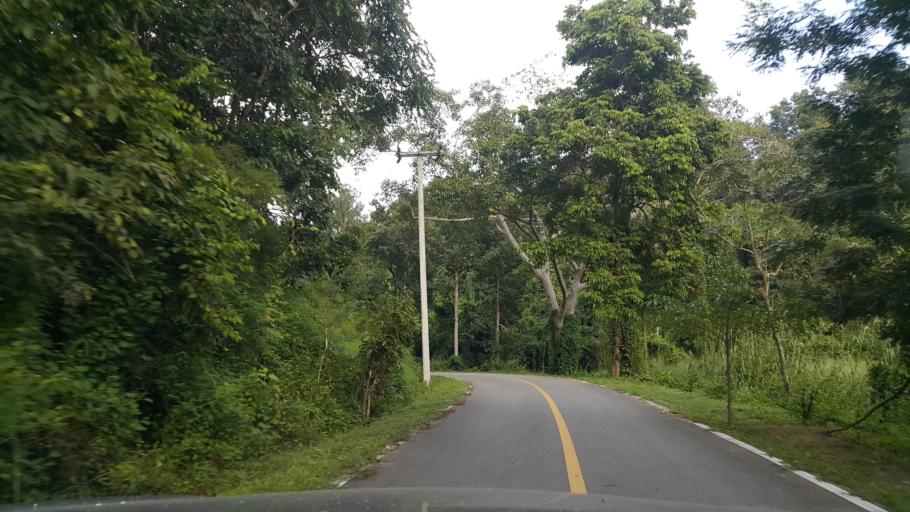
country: TH
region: Chiang Mai
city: San Sai
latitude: 18.9463
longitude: 99.0641
